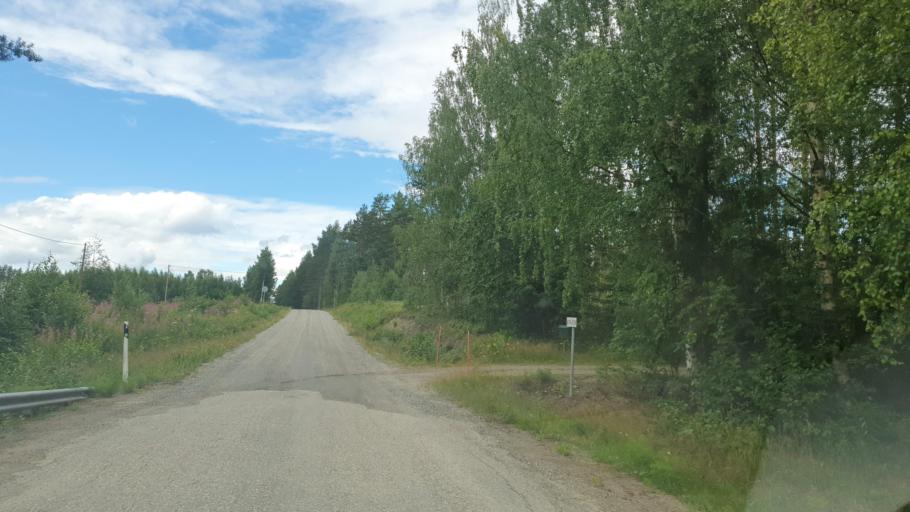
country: FI
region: Kainuu
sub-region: Kehys-Kainuu
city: Kuhmo
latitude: 64.1087
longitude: 29.3853
